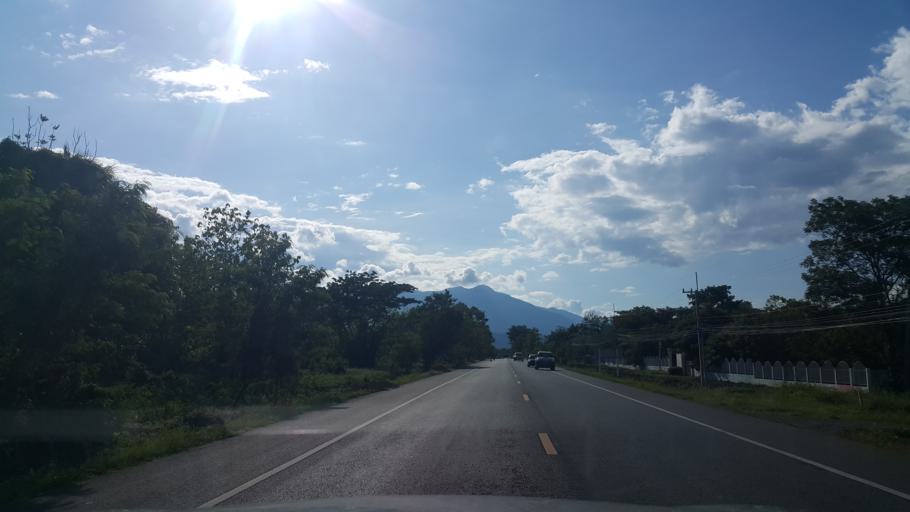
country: TH
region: Phayao
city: Phayao
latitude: 19.0809
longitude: 99.8633
